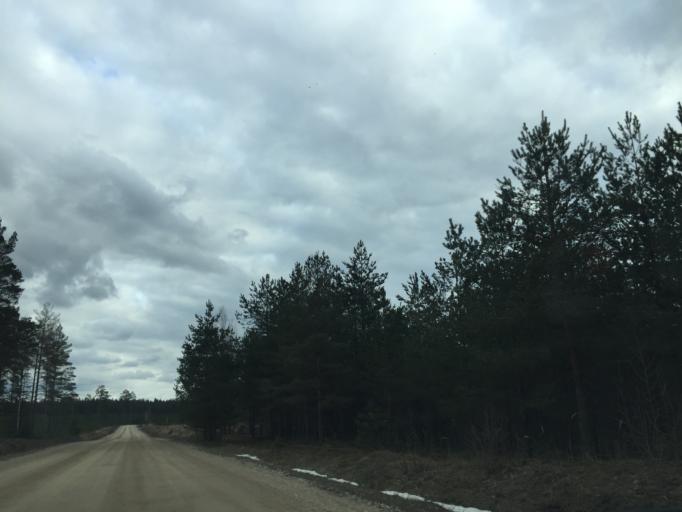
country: LV
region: Jaunjelgava
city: Jaunjelgava
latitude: 56.5830
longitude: 25.0045
